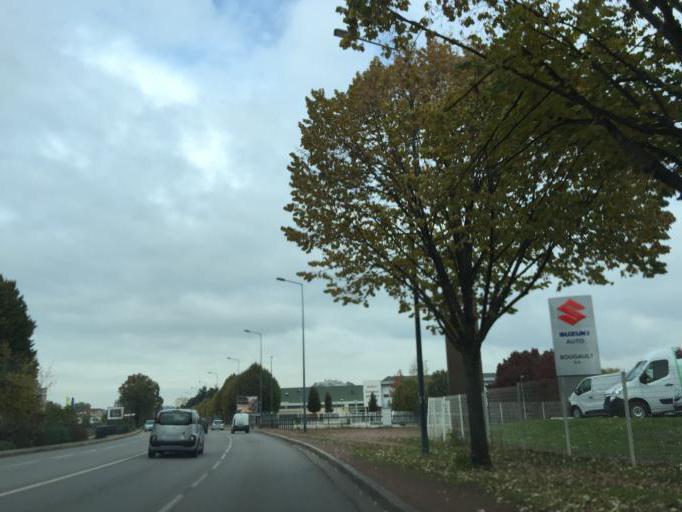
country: FR
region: Rhone-Alpes
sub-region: Departement de la Loire
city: Saint-Priest-en-Jarez
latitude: 45.4591
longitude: 4.3860
